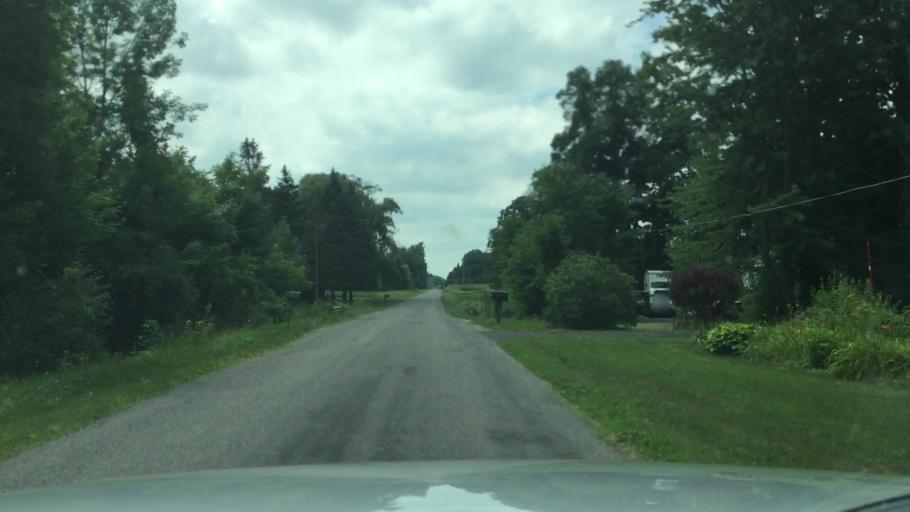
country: US
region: Michigan
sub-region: Saginaw County
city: Birch Run
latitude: 43.3006
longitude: -83.8348
